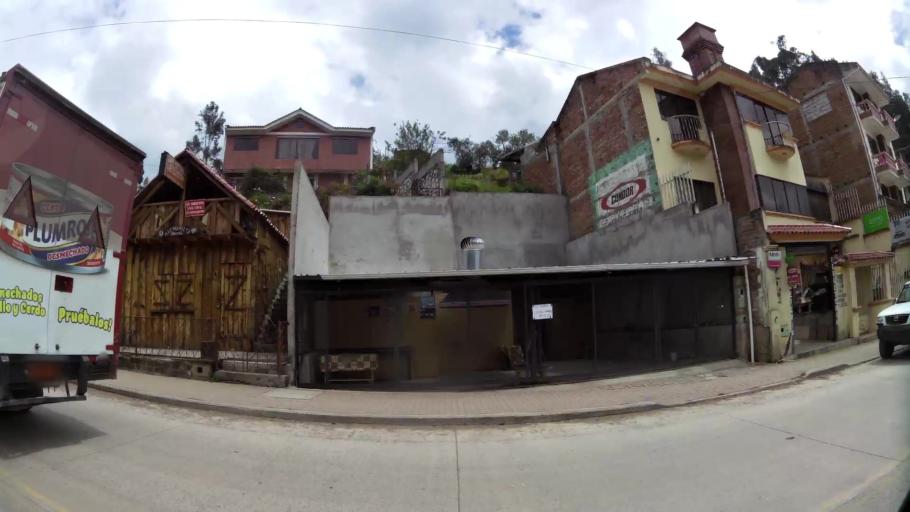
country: EC
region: Azuay
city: Cuenca
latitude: -2.8720
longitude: -79.0763
